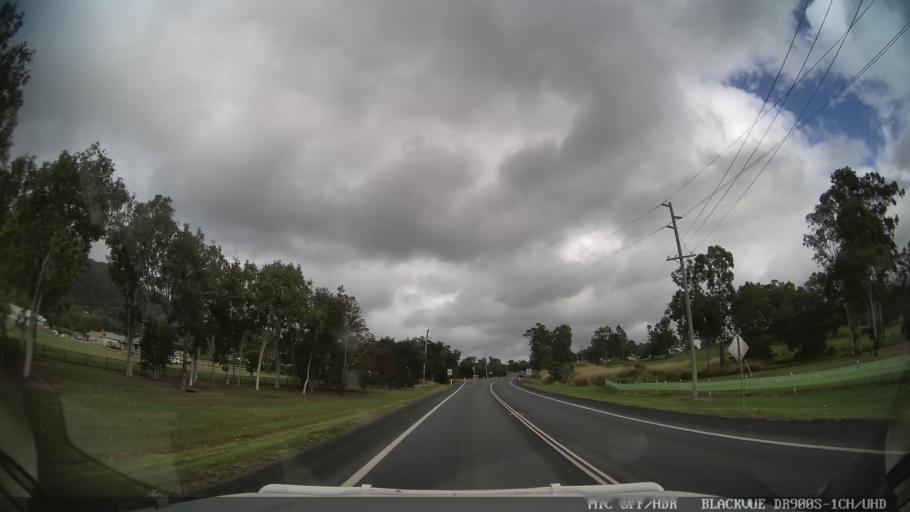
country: AU
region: Queensland
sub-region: Whitsunday
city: Proserpine
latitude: -20.3028
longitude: 148.6671
